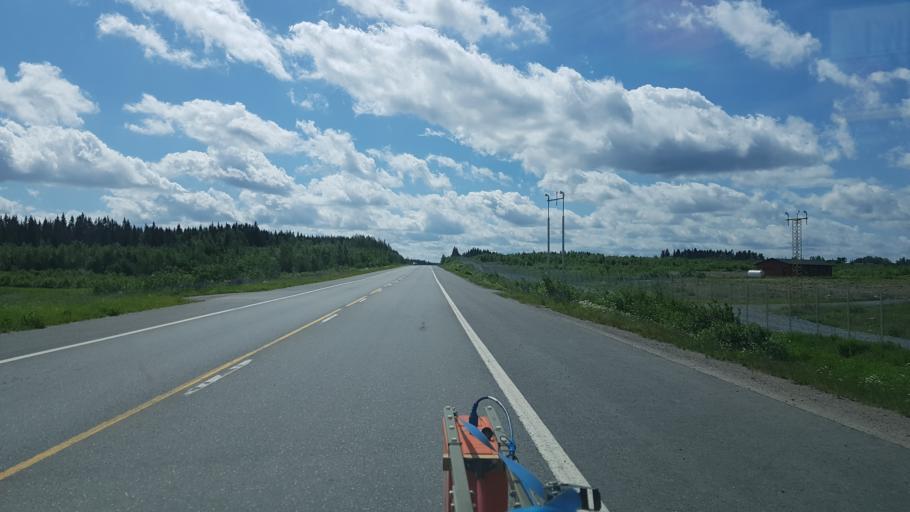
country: FI
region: Pirkanmaa
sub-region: Tampere
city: Pirkkala
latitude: 61.4216
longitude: 23.6345
